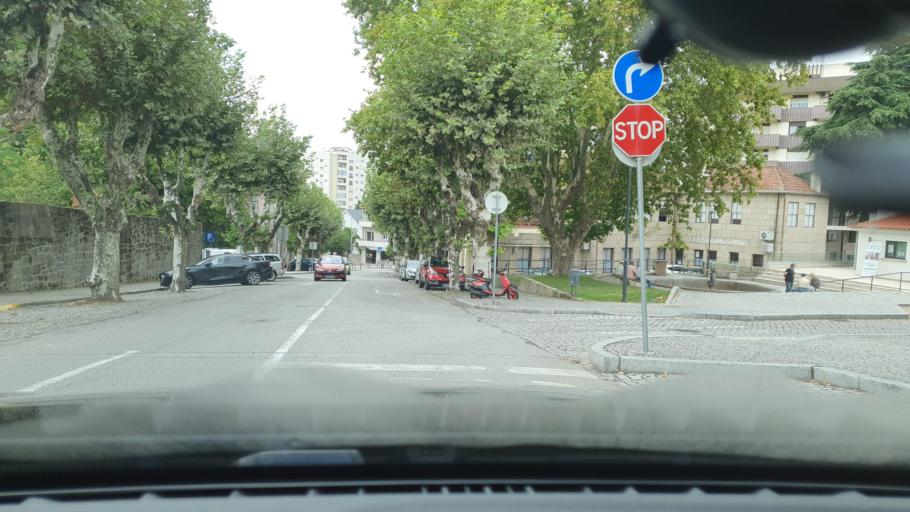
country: PT
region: Vila Real
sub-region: Chaves
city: Chaves
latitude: 41.7411
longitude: -7.4728
